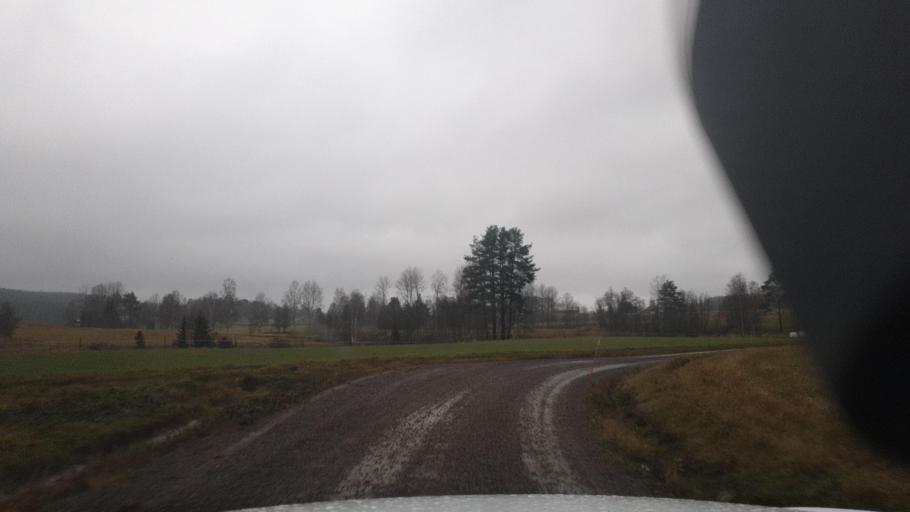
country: SE
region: Vaermland
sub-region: Eda Kommun
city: Charlottenberg
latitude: 59.7402
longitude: 12.1484
